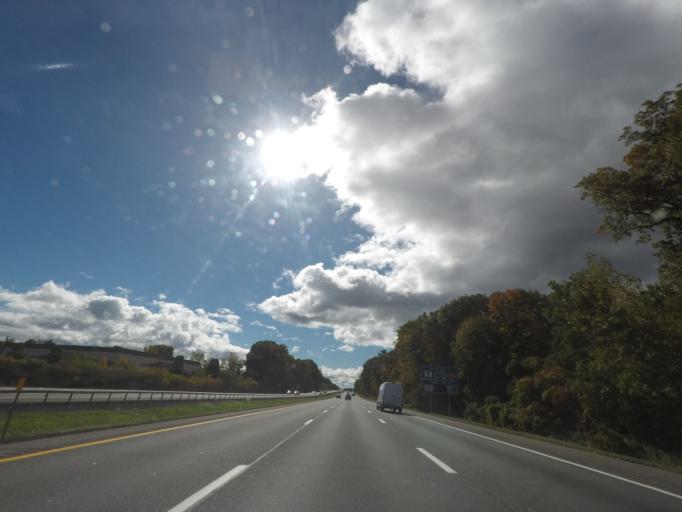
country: US
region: New York
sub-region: Saratoga County
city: Country Knolls
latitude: 42.8741
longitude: -73.7773
